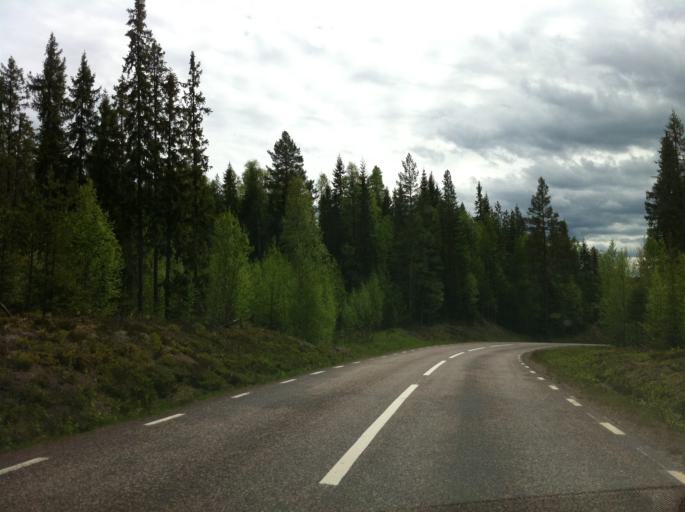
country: SE
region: Dalarna
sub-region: Malung-Saelens kommun
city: Malung
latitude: 61.2963
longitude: 13.1378
